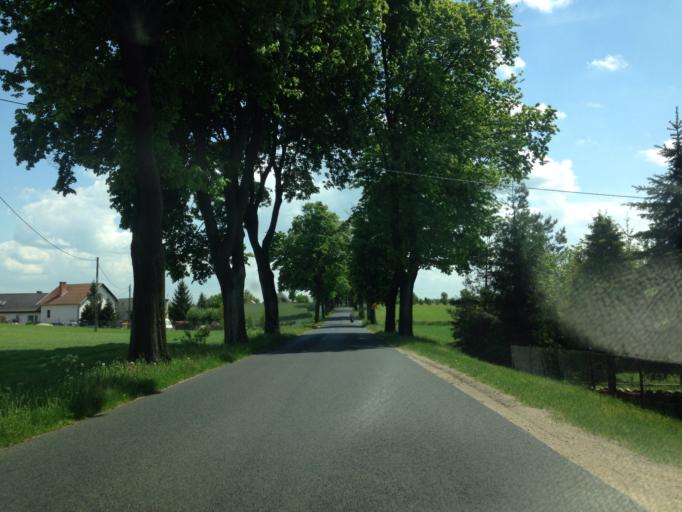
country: PL
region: Kujawsko-Pomorskie
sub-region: Powiat brodnicki
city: Brodnica
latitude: 53.3202
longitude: 19.3806
